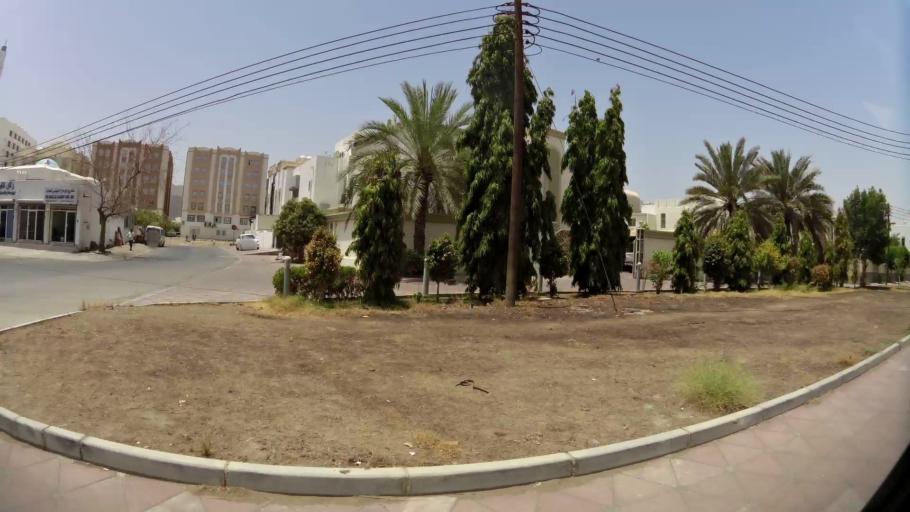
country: OM
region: Muhafazat Masqat
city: Bawshar
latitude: 23.5850
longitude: 58.4241
